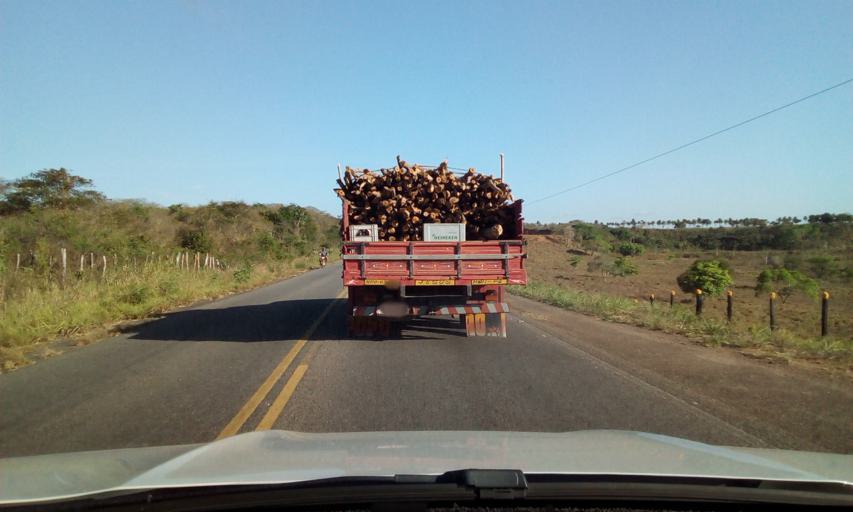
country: BR
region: Paraiba
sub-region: Mari
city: Mari
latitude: -7.0127
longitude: -35.3608
